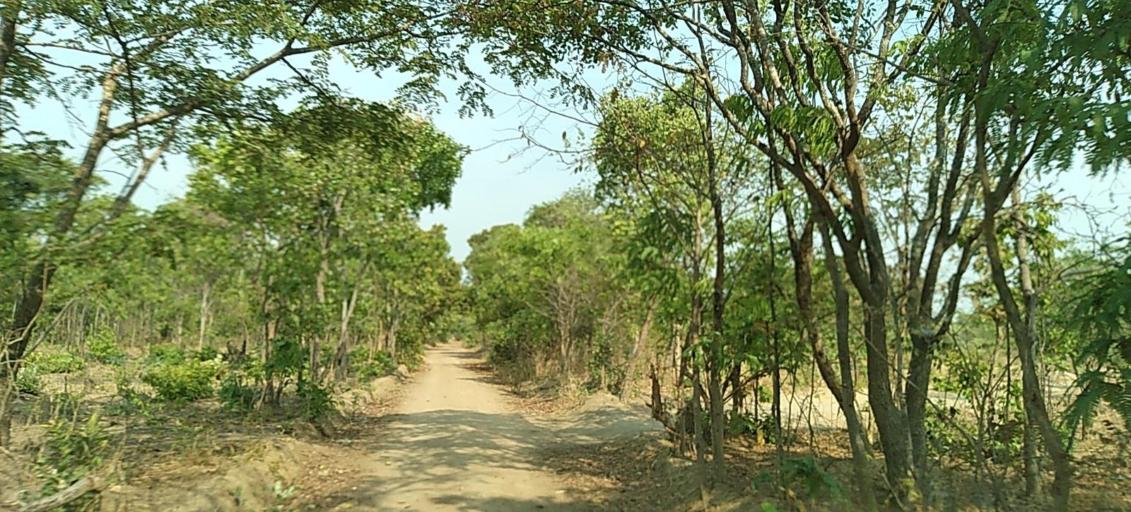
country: ZM
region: Copperbelt
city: Luanshya
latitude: -13.2206
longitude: 28.6643
